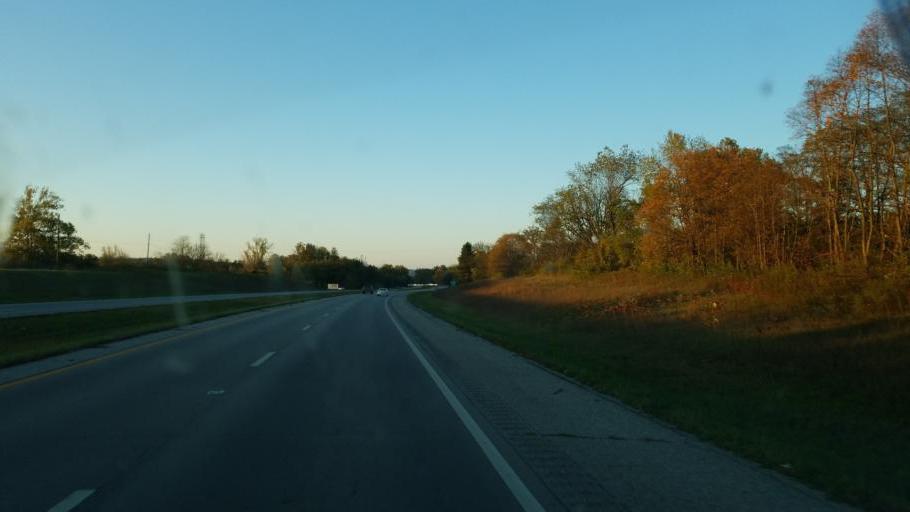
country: US
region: Ohio
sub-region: Pike County
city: Piketon
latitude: 39.0246
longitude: -83.0266
